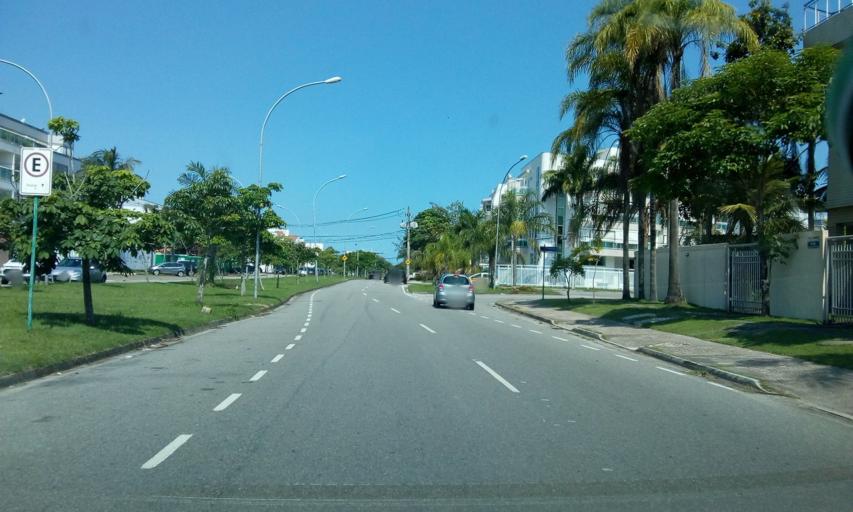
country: BR
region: Rio de Janeiro
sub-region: Nilopolis
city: Nilopolis
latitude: -23.0119
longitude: -43.4512
